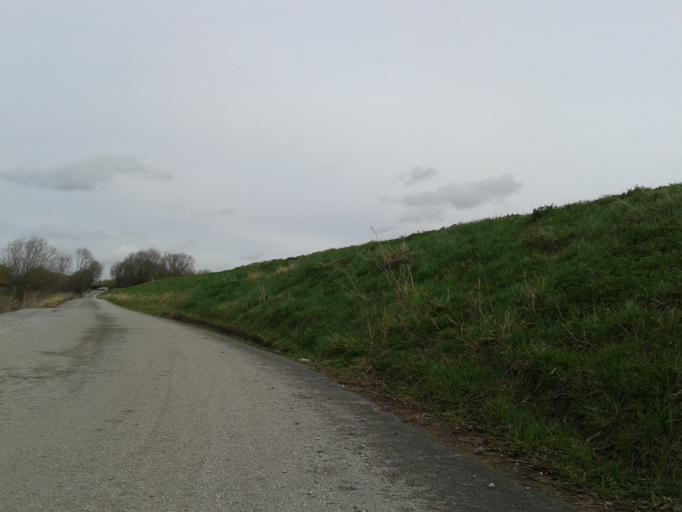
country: GB
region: England
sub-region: Cambridgeshire
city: Ely
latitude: 52.3880
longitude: 0.2672
